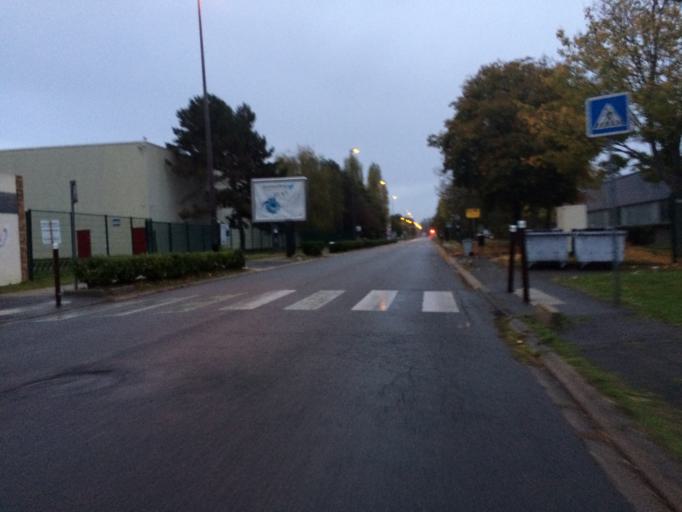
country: FR
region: Ile-de-France
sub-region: Departement de l'Essonne
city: Orsay
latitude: 48.6886
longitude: 2.2020
